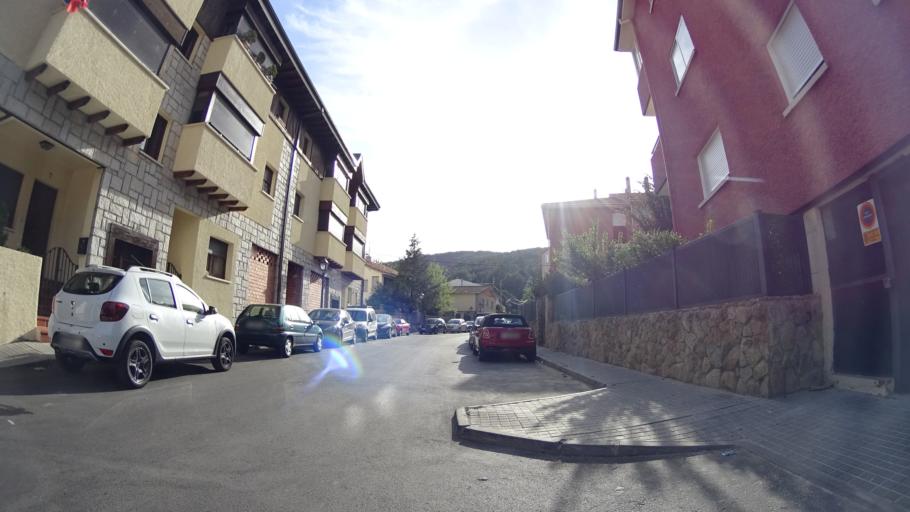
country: ES
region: Madrid
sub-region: Provincia de Madrid
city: Navacerrada
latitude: 40.7291
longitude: -4.0162
